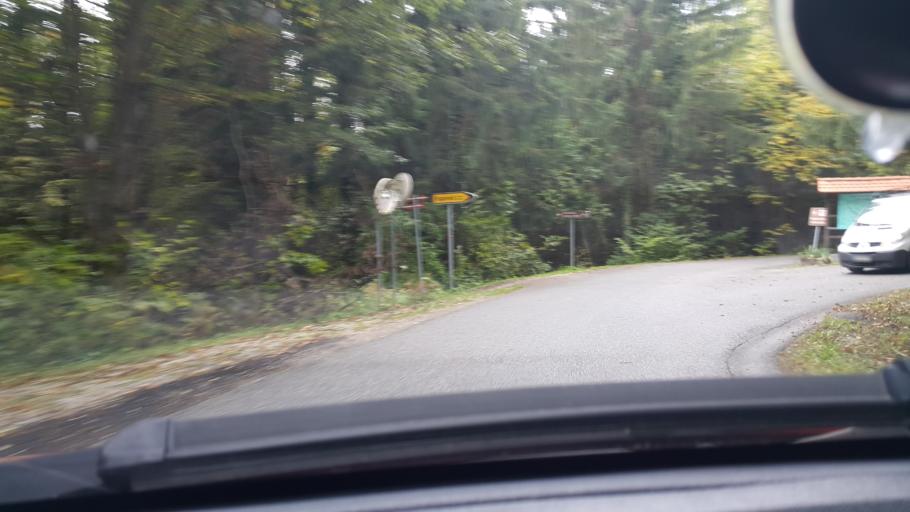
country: SI
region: Race-Fram
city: Morje
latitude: 46.4536
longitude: 15.6117
